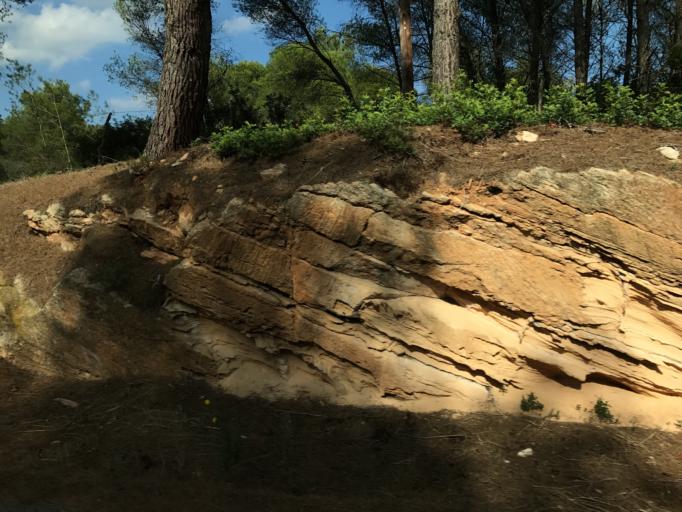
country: ES
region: Balearic Islands
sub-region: Illes Balears
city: Santa Margalida
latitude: 39.7295
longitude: 3.1939
